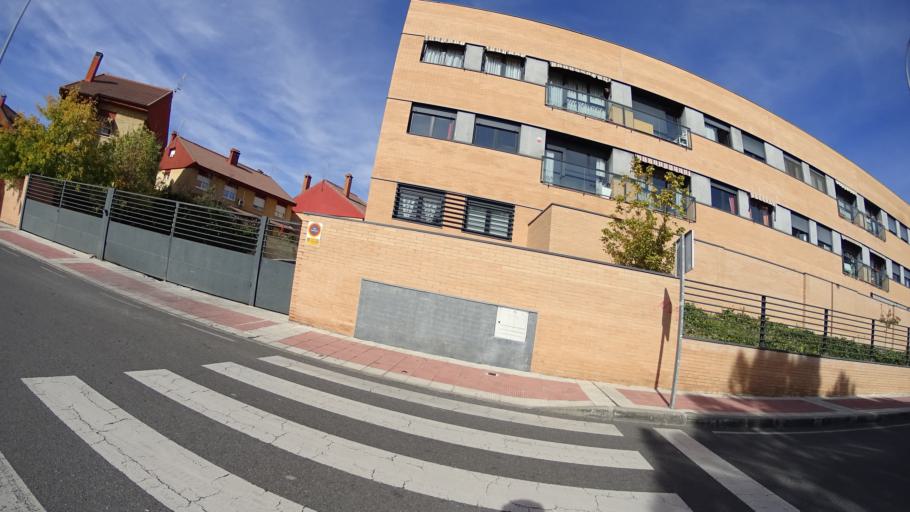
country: ES
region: Madrid
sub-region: Provincia de Madrid
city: Collado-Villalba
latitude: 40.6237
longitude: -4.0170
